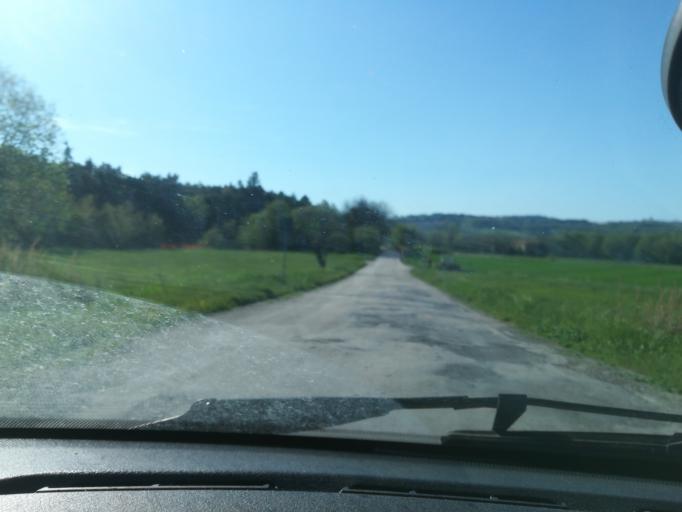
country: IT
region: The Marches
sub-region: Provincia di Macerata
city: Zona Industriale
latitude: 43.2676
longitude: 13.4930
